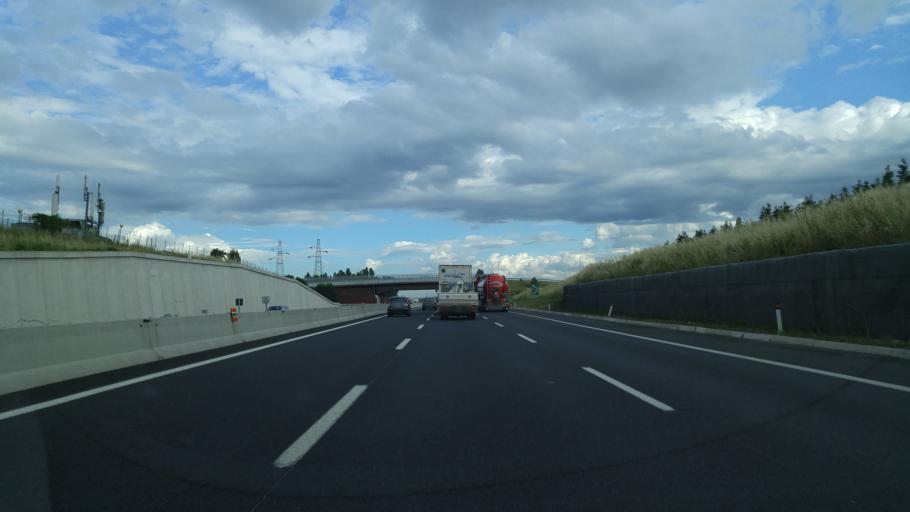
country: IT
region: Emilia-Romagna
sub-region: Provincia di Rimini
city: Rivazzurra
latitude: 44.0089
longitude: 12.5963
